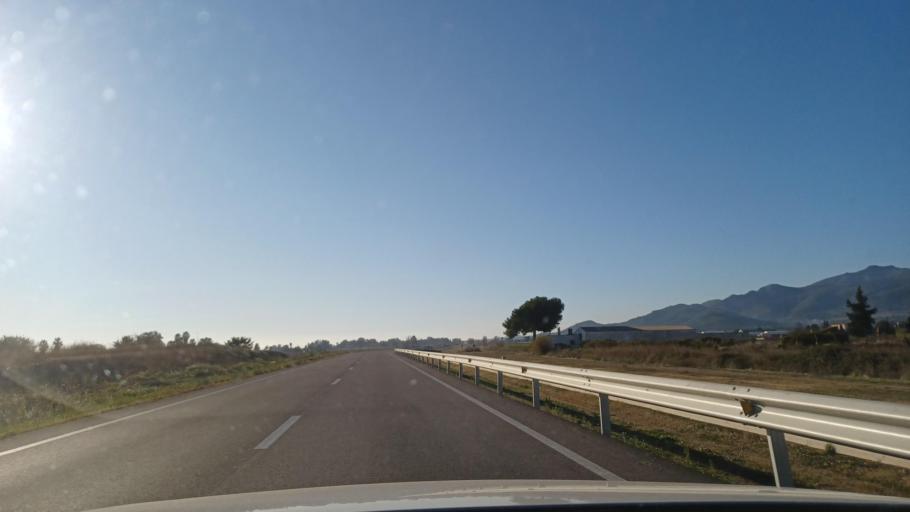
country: ES
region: Catalonia
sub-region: Provincia de Tarragona
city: Amposta
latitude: 40.6931
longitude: 0.5900
